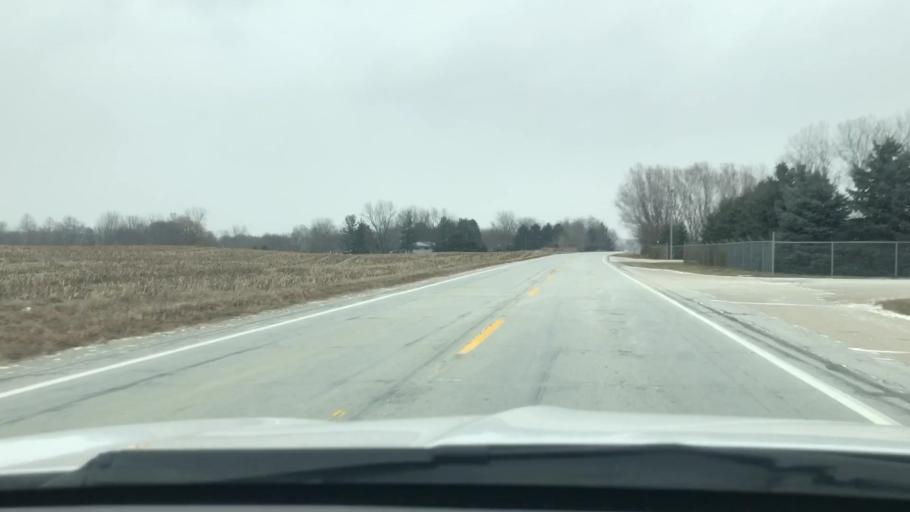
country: US
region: Indiana
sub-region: Fulton County
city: Akron
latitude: 41.0395
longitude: -86.0805
